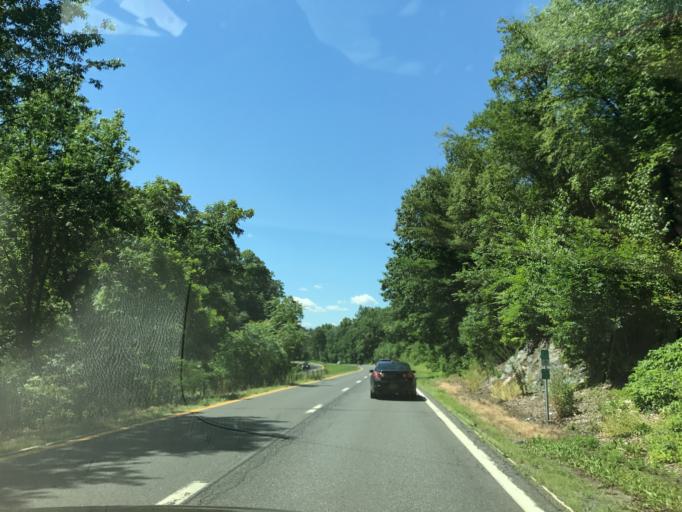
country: US
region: New York
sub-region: Dutchess County
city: Pleasant Valley
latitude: 41.7212
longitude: -73.7830
